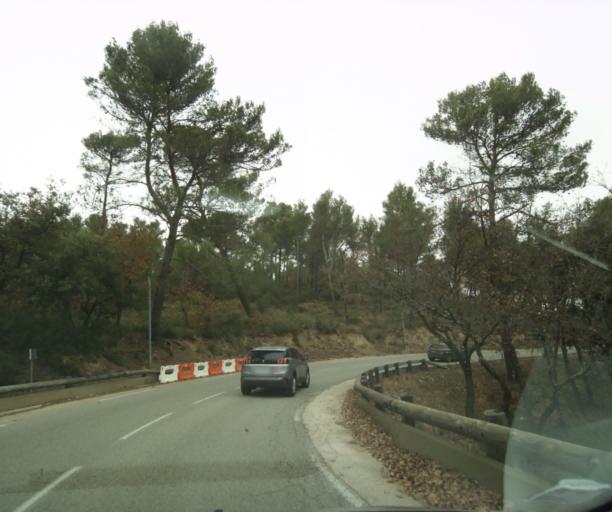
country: FR
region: Provence-Alpes-Cote d'Azur
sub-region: Departement des Bouches-du-Rhone
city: Peynier
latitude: 43.4330
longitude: 5.6258
